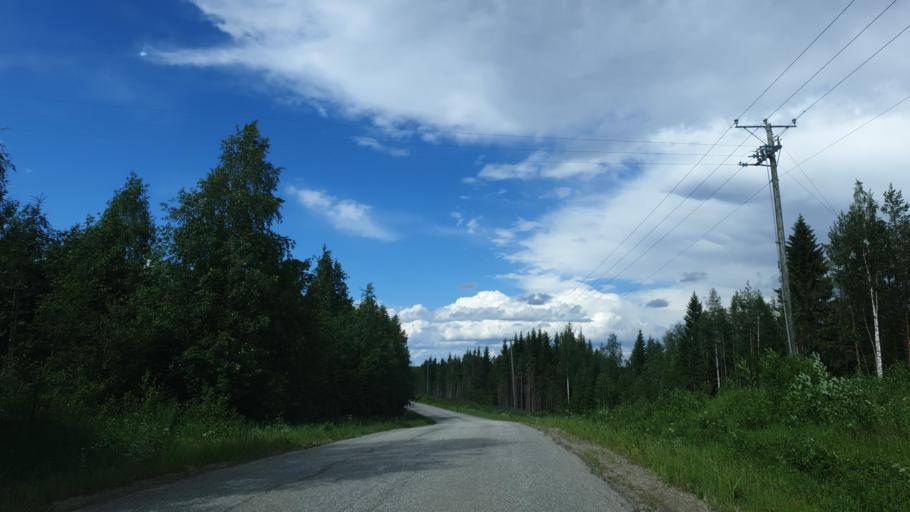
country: FI
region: Northern Savo
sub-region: Koillis-Savo
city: Kaavi
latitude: 62.9799
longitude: 28.7453
